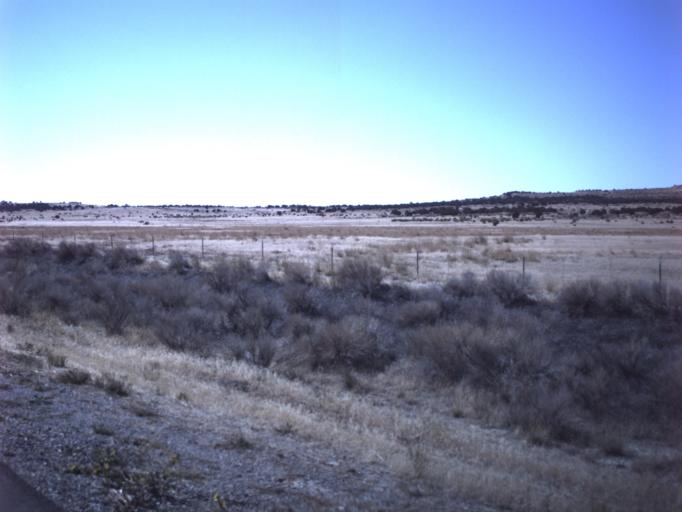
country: US
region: Utah
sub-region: Tooele County
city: Grantsville
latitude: 40.2576
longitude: -112.7403
